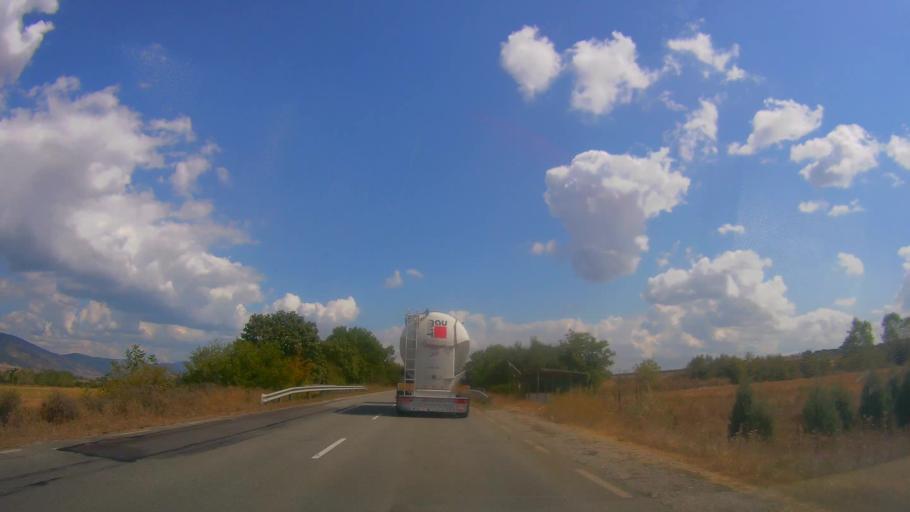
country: BG
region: Sliven
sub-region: Obshtina Tvurditsa
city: Tvurditsa
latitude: 42.6569
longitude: 25.9257
